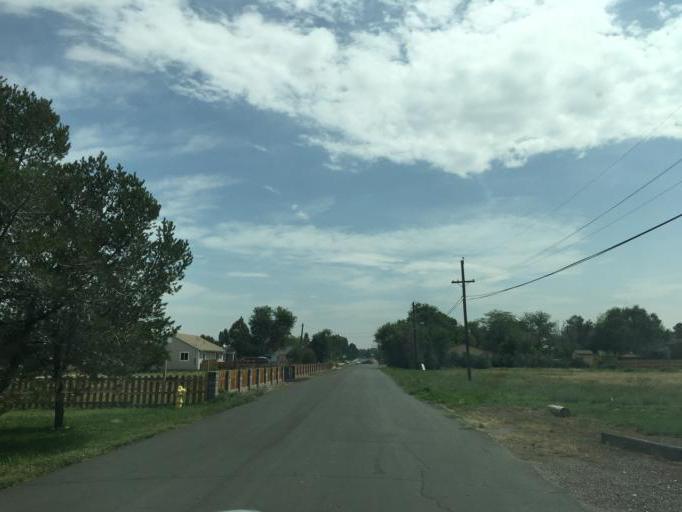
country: US
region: Colorado
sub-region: Adams County
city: Aurora
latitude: 39.7337
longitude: -104.8034
